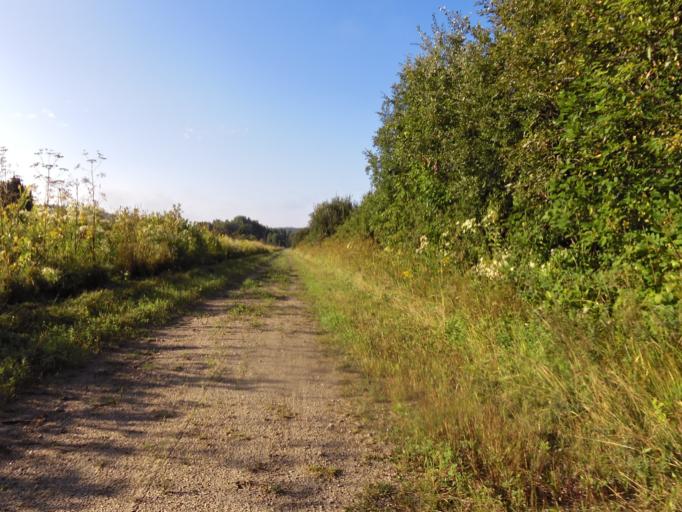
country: CA
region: Quebec
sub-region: Outaouais
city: Maniwaki
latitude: 46.2965
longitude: -76.0241
